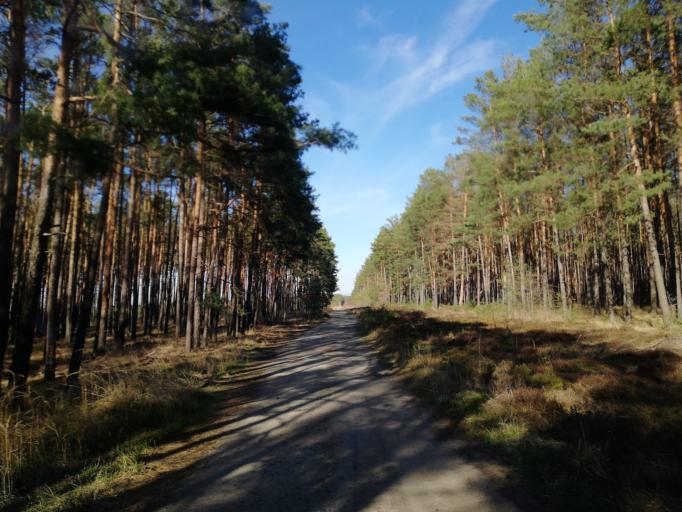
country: DE
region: Brandenburg
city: Ruckersdorf
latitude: 51.5686
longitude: 13.5937
